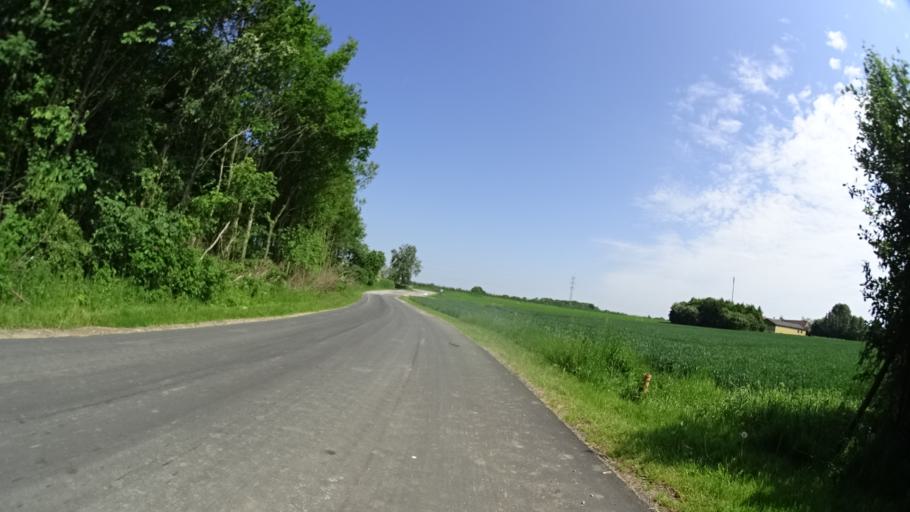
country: DK
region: Central Jutland
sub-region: Arhus Kommune
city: Kolt
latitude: 56.1177
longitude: 10.0513
